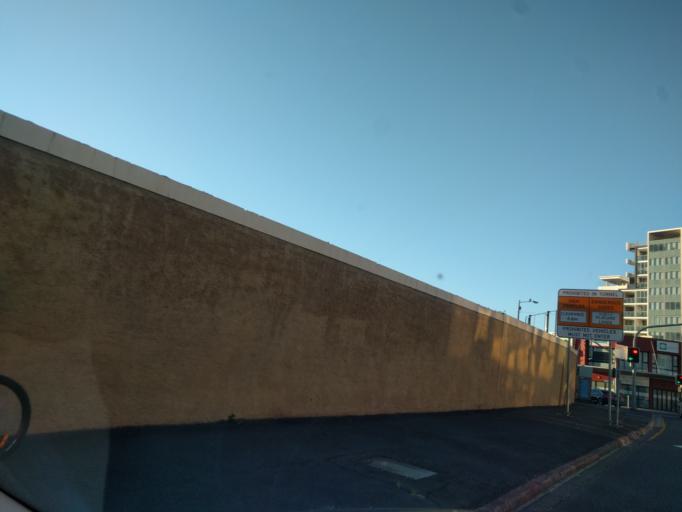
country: AU
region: Queensland
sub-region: Brisbane
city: Fortitude Valley
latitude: -27.4491
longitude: 153.0351
